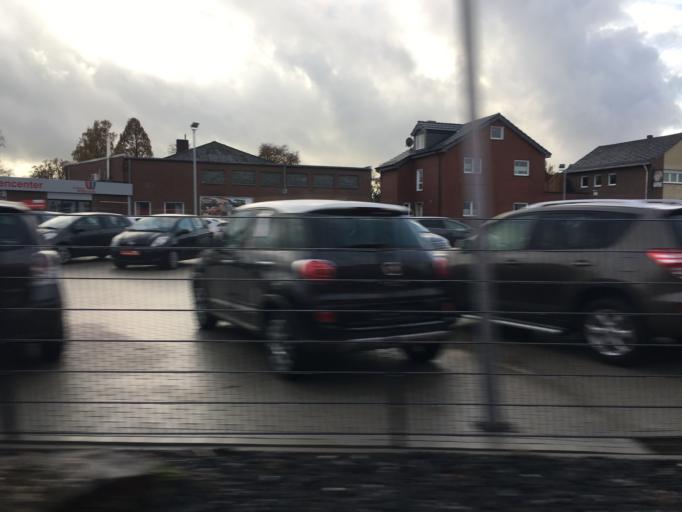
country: DE
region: North Rhine-Westphalia
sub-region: Regierungsbezirk Munster
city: Steinfurt
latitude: 52.1192
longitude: 7.3949
